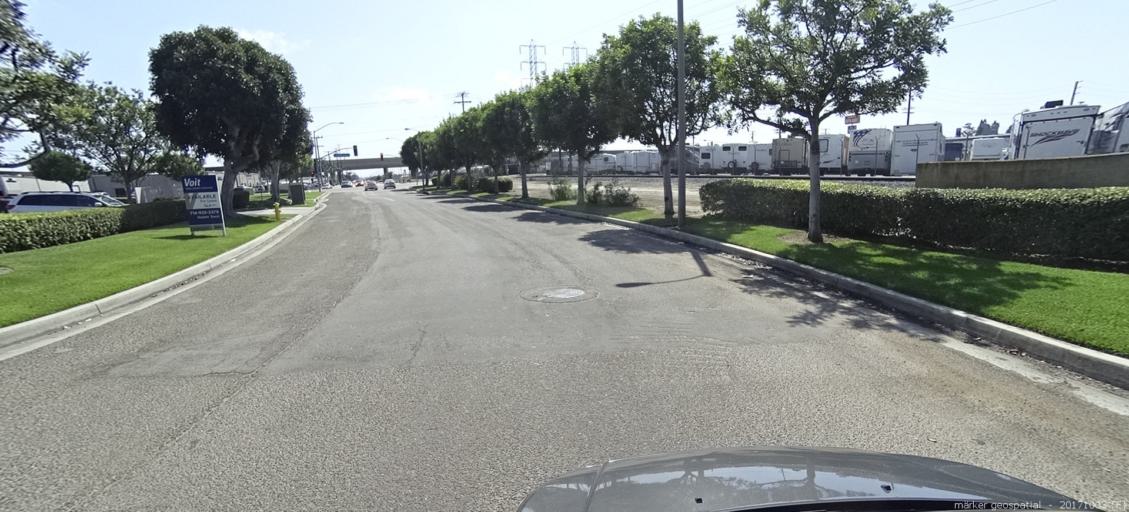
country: US
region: California
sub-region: Orange County
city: Westminster
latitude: 33.7748
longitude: -117.9986
